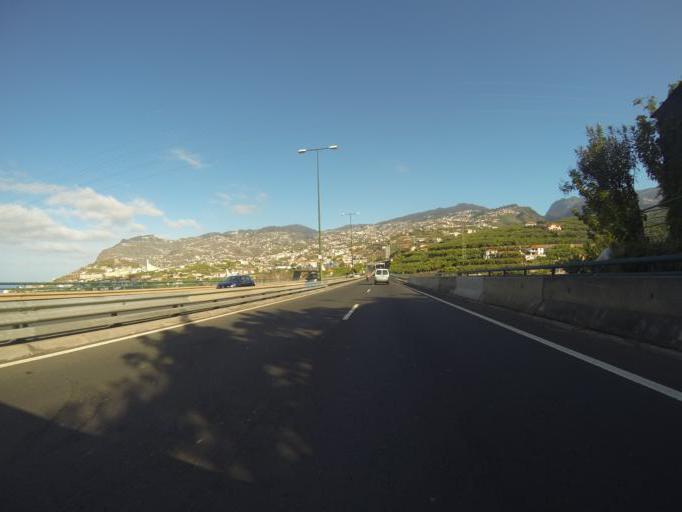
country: PT
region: Madeira
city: Camara de Lobos
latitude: 32.6509
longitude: -16.9601
